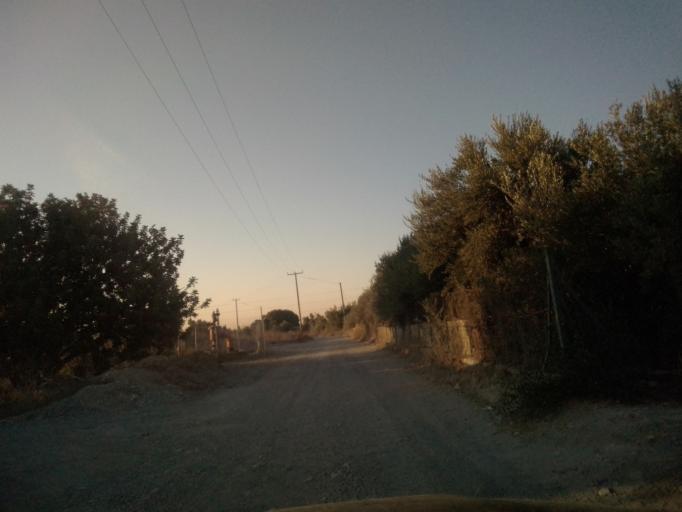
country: CY
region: Limassol
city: Ypsonas
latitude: 34.6696
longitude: 32.9660
